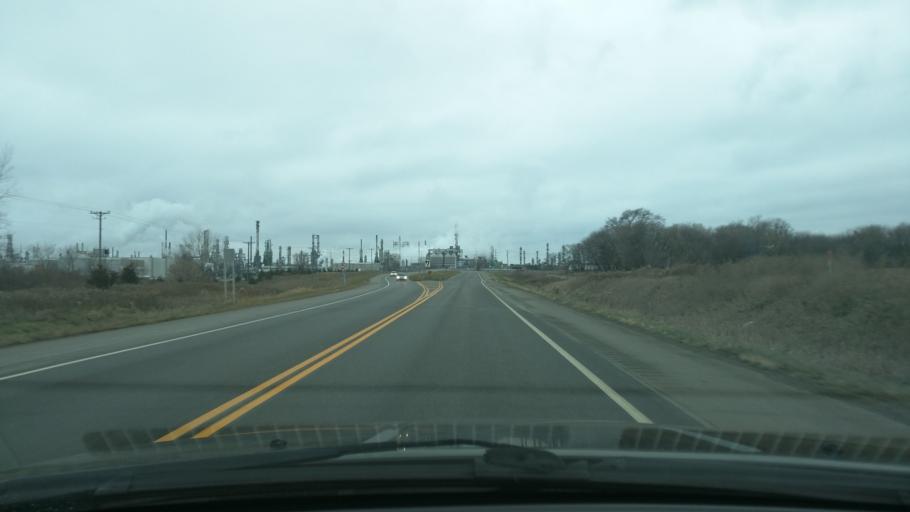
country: US
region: Minnesota
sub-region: Washington County
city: Saint Paul Park
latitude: 44.7617
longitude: -93.0246
